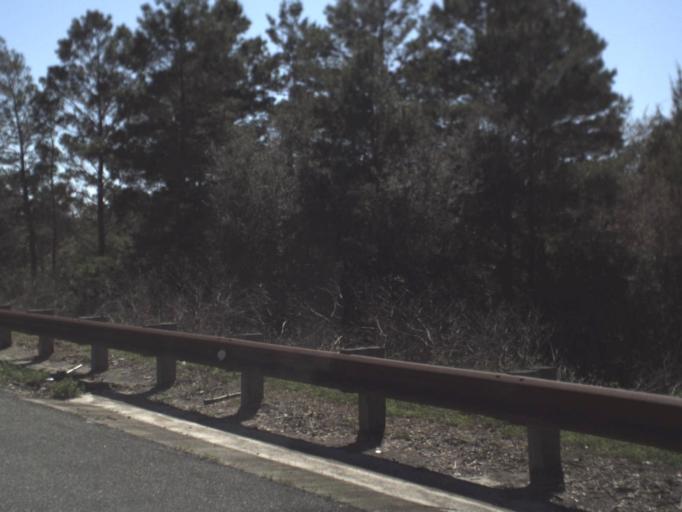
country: US
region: Florida
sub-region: Gulf County
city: Port Saint Joe
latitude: 29.8732
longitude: -85.3395
